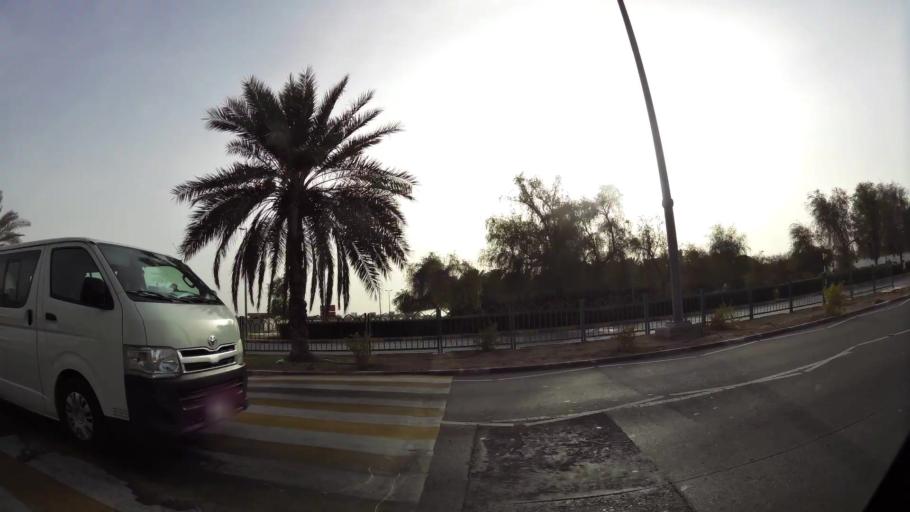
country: AE
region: Abu Dhabi
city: Al Ain
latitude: 24.2343
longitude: 55.7196
